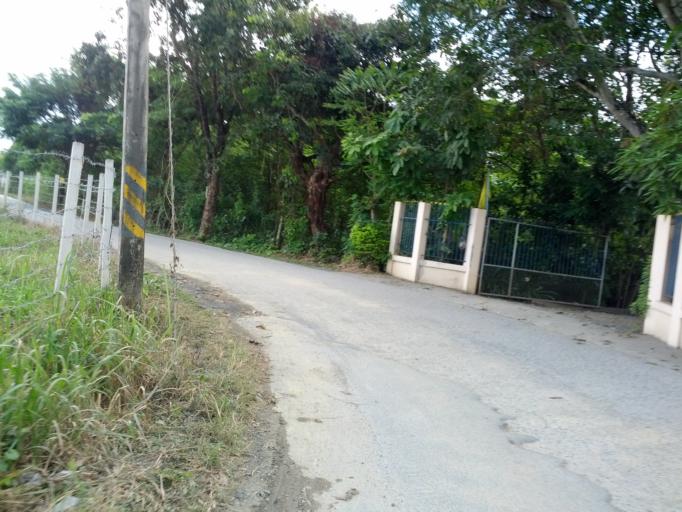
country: TH
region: Chiang Mai
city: San Kamphaeng
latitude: 18.7954
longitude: 99.1033
